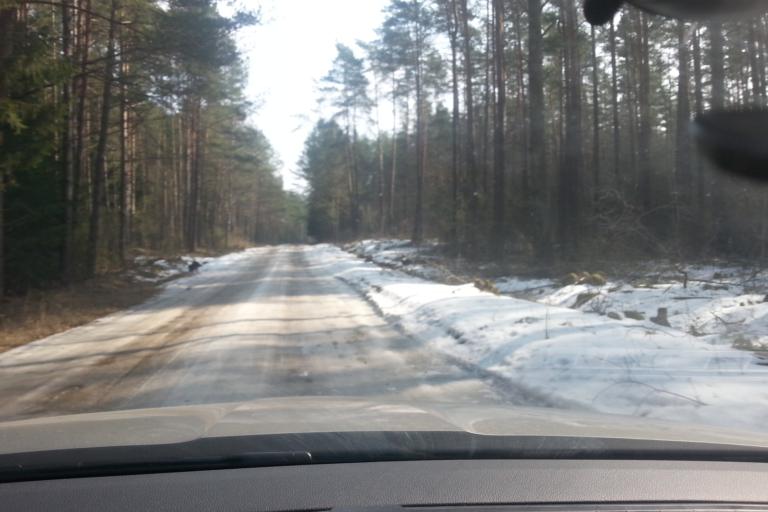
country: LT
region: Vilnius County
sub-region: Trakai
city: Rudiskes
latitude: 54.5093
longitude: 24.9373
